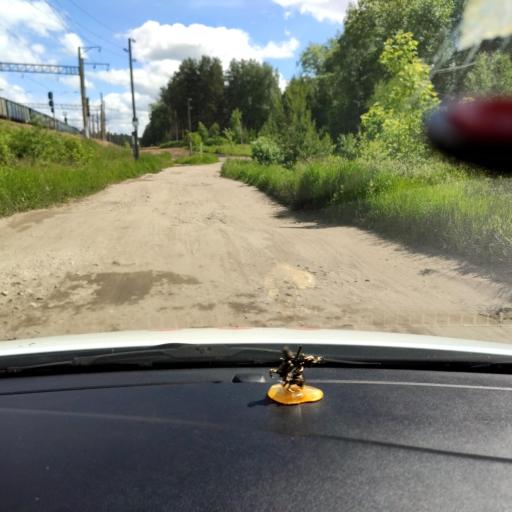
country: RU
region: Tatarstan
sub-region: Zelenodol'skiy Rayon
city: Vasil'yevo
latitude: 55.8397
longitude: 48.7196
